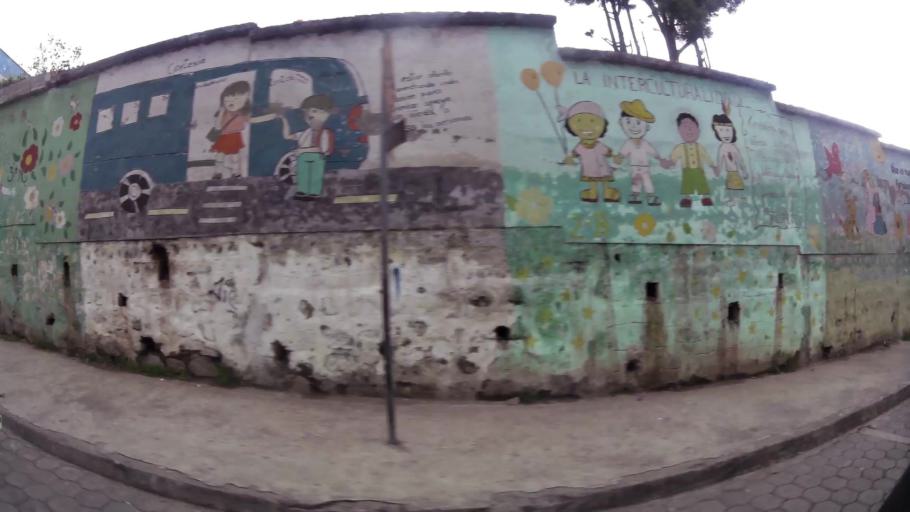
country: EC
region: Pichincha
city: Quito
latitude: -0.2993
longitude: -78.5244
